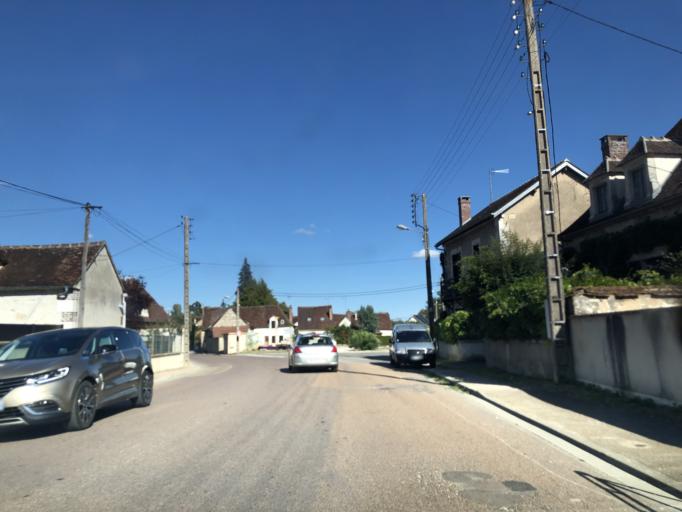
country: FR
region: Bourgogne
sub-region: Departement de l'Yonne
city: Appoigny
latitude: 47.8767
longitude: 3.5325
